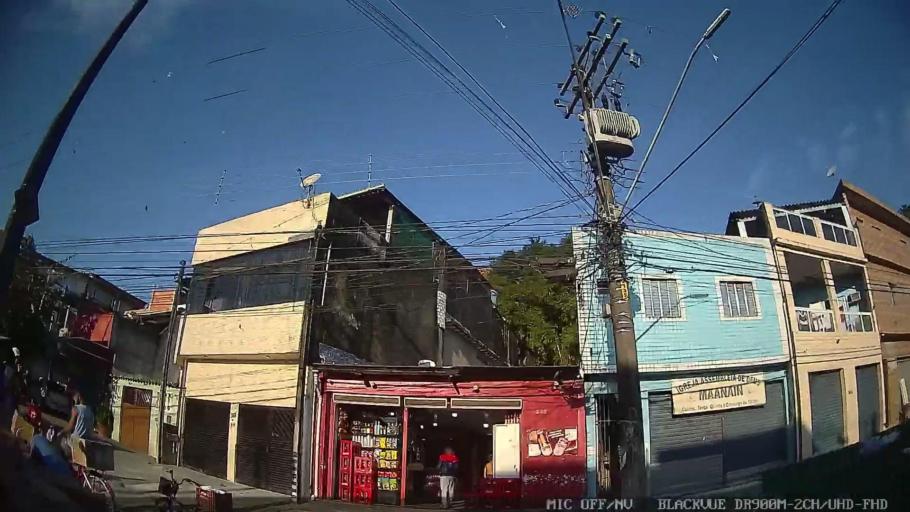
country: BR
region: Sao Paulo
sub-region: Guaruja
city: Guaruja
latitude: -23.9776
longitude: -46.2599
